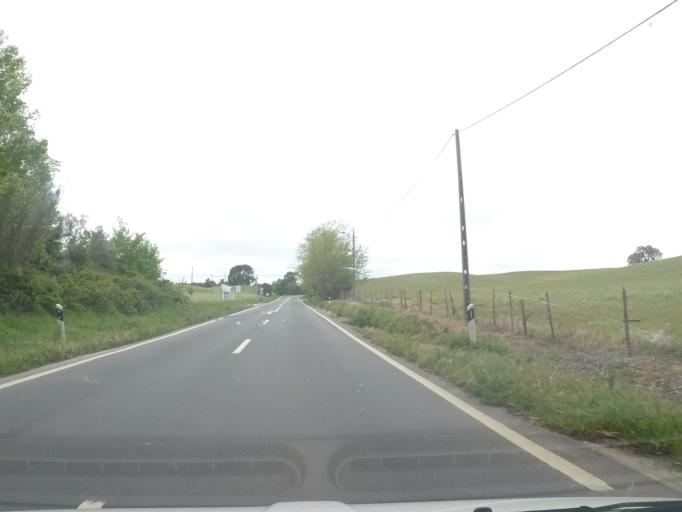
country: PT
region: Setubal
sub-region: Santiago do Cacem
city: Cercal
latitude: 37.8232
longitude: -8.6902
